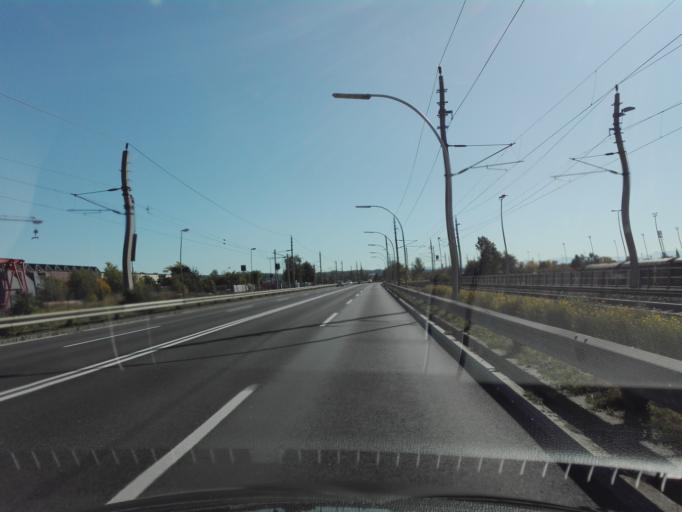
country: AT
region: Upper Austria
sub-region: Linz Stadt
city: Linz
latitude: 48.2686
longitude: 14.3210
